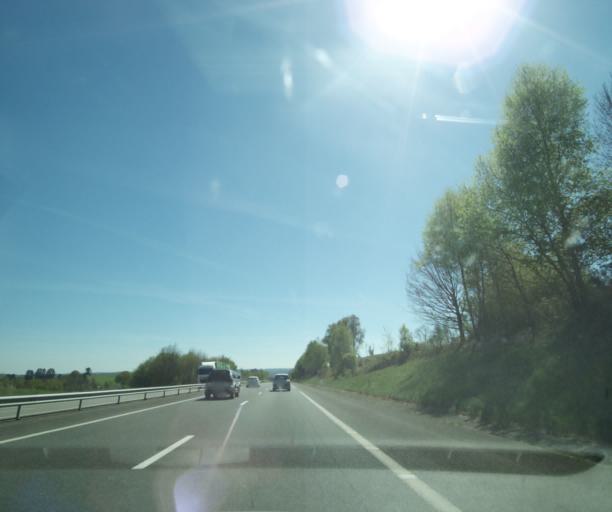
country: FR
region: Limousin
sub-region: Departement de la Correze
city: Uzerche
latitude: 45.4492
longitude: 1.5089
